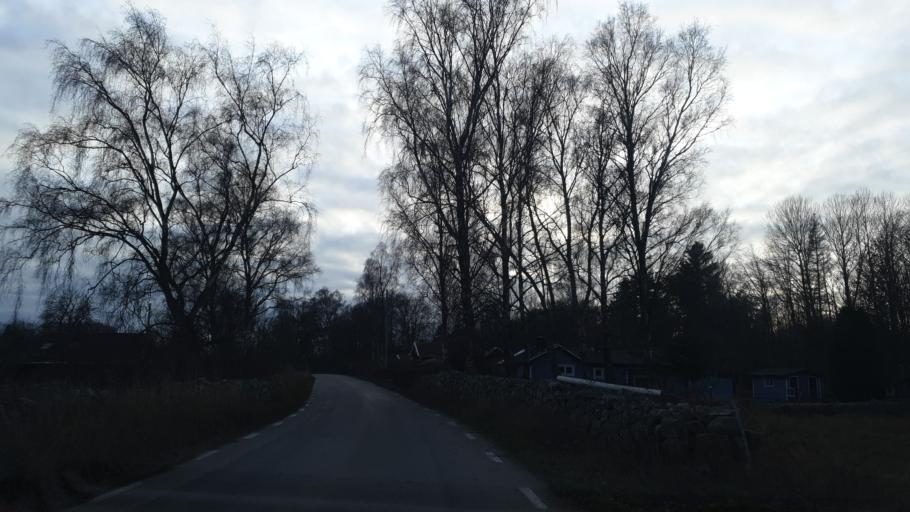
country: SE
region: Blekinge
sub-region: Karlskrona Kommun
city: Jaemjoe
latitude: 56.1724
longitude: 15.9316
